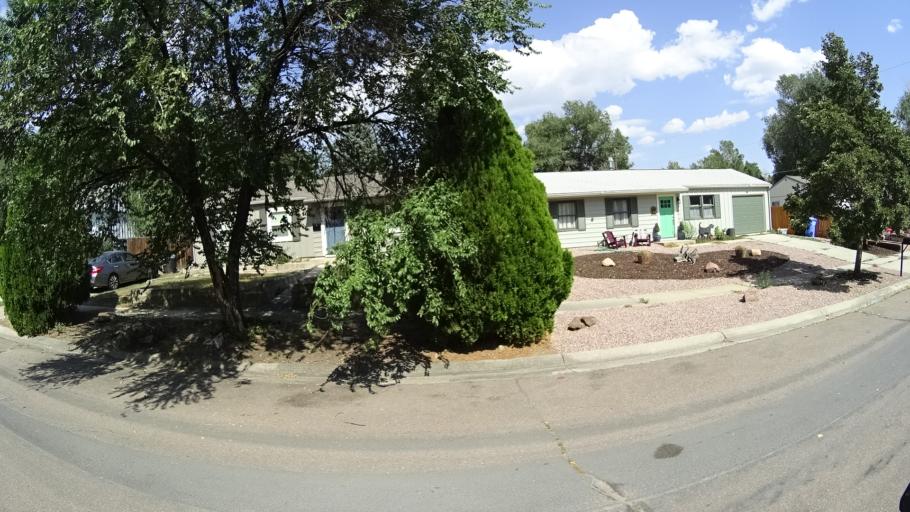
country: US
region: Colorado
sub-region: El Paso County
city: Colorado Springs
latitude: 38.8319
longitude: -104.7722
